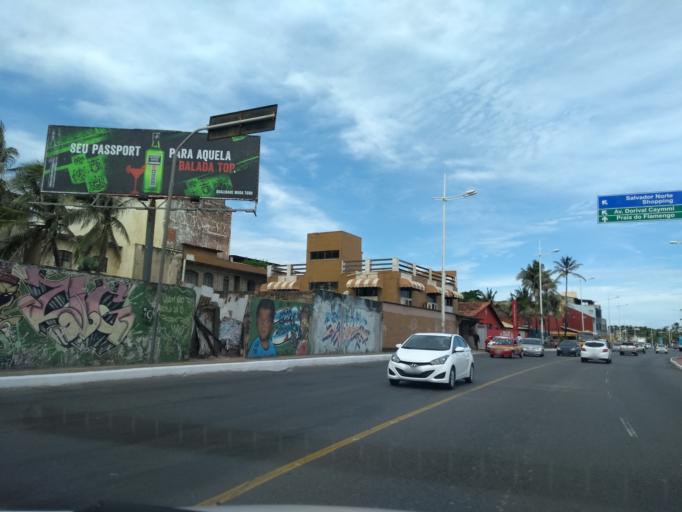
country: BR
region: Bahia
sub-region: Lauro De Freitas
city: Lauro de Freitas
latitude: -12.9505
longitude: -38.3695
